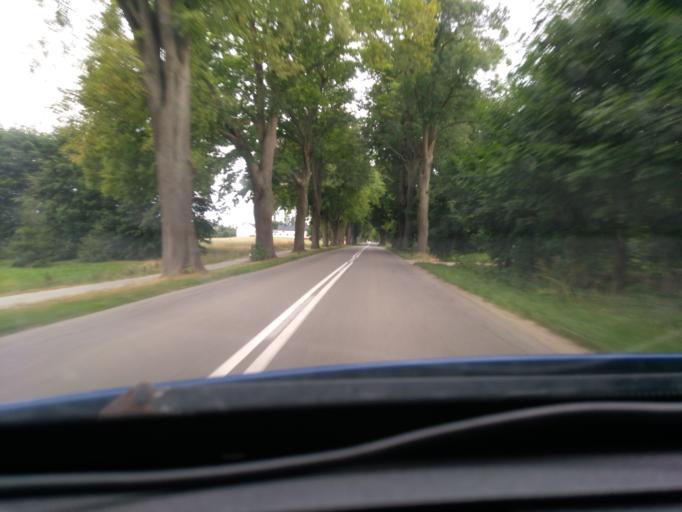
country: PL
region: Pomeranian Voivodeship
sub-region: Powiat kartuski
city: Banino
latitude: 54.3767
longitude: 18.3741
